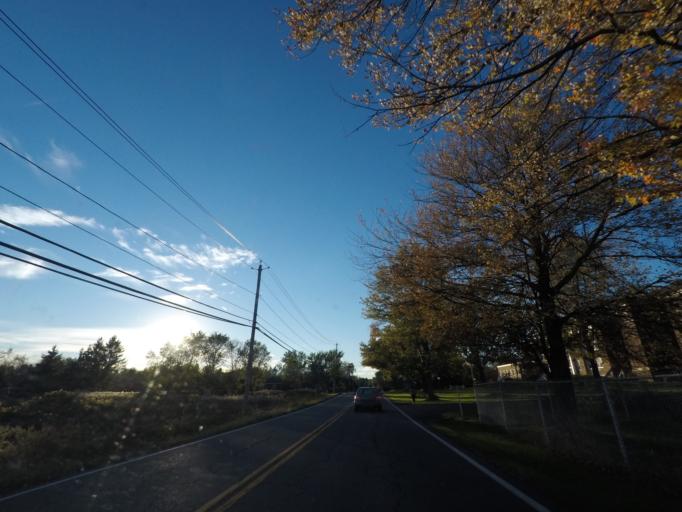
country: US
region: New York
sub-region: Albany County
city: Watervliet
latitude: 42.7469
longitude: -73.7174
